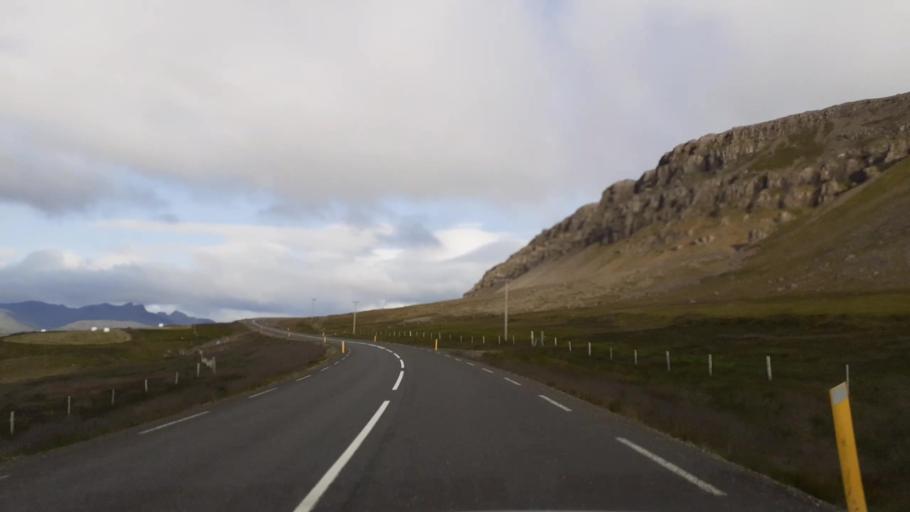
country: IS
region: East
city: Eskifjoerdur
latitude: 64.7982
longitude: -13.9698
